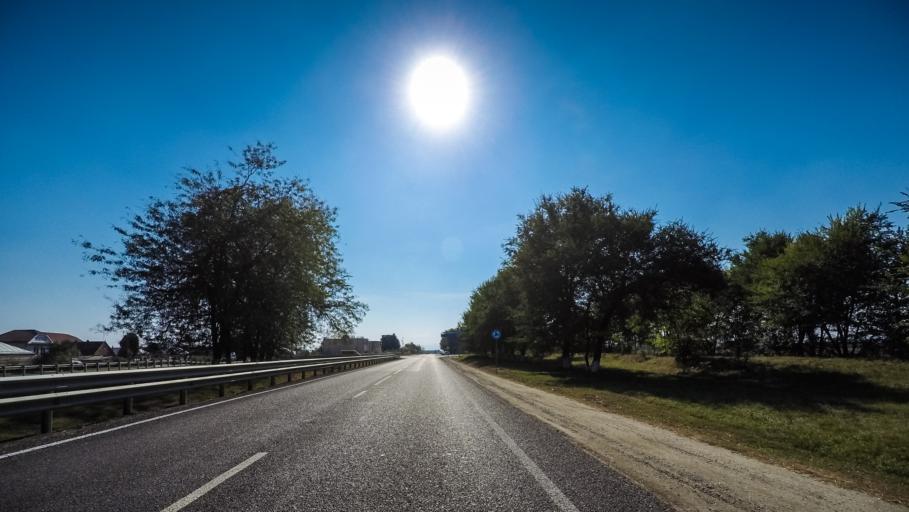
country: RU
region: Kabardino-Balkariya
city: Chegem Vtoroy
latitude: 43.5820
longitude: 43.5805
